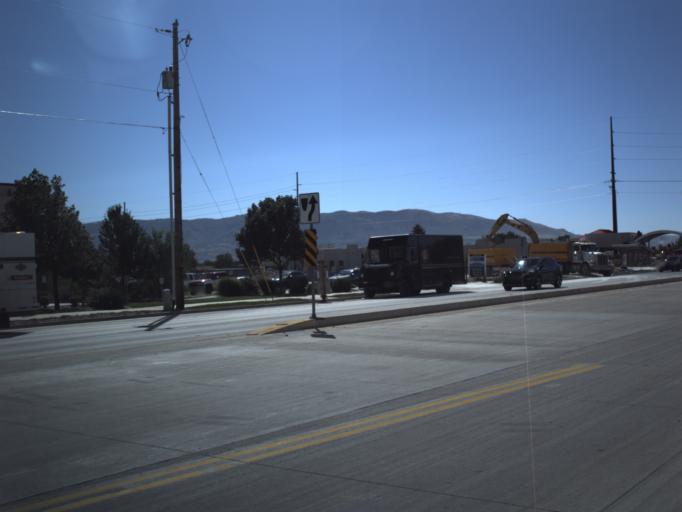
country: US
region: Utah
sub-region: Salt Lake County
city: South Jordan
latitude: 40.5462
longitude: -111.9388
